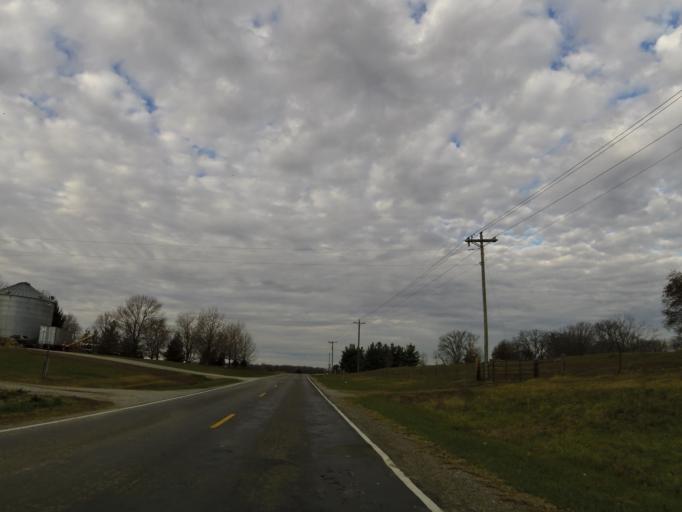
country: US
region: Illinois
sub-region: Jefferson County
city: Mount Vernon
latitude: 38.3713
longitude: -88.9997
